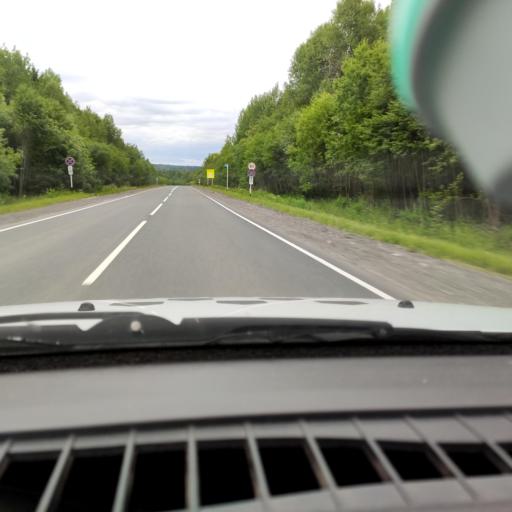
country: RU
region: Perm
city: Chusovoy
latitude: 58.2103
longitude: 57.8156
